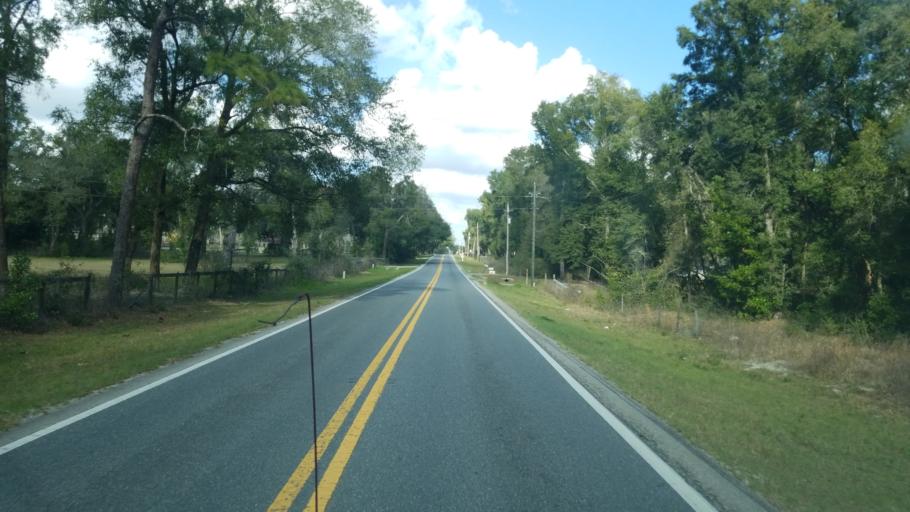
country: US
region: Florida
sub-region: Marion County
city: Belleview
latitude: 28.9637
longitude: -82.1199
